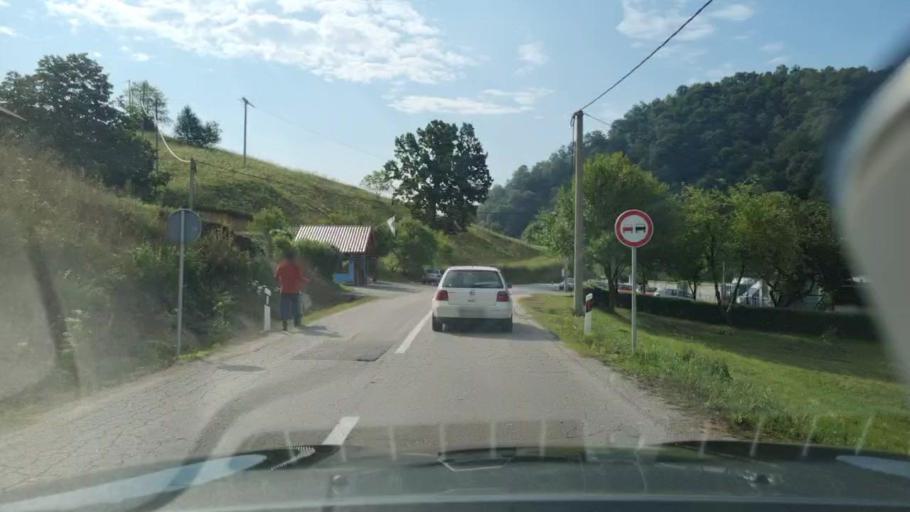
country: BA
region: Federation of Bosnia and Herzegovina
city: Otoka
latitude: 44.9983
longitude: 16.1504
